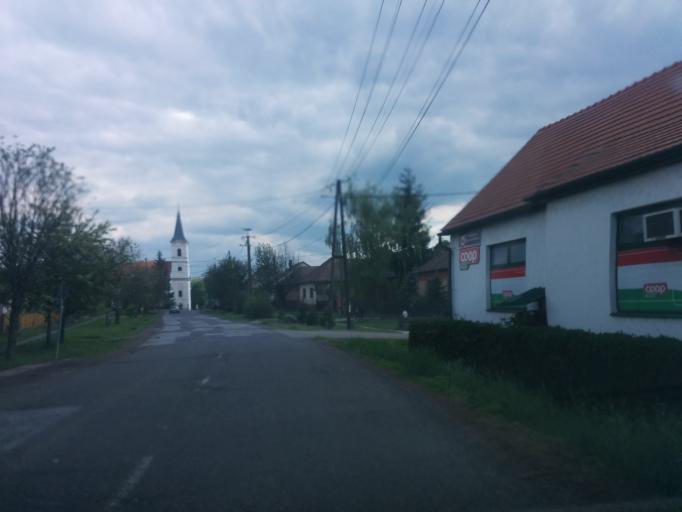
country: HU
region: Nograd
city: Bercel
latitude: 47.8485
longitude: 19.3888
